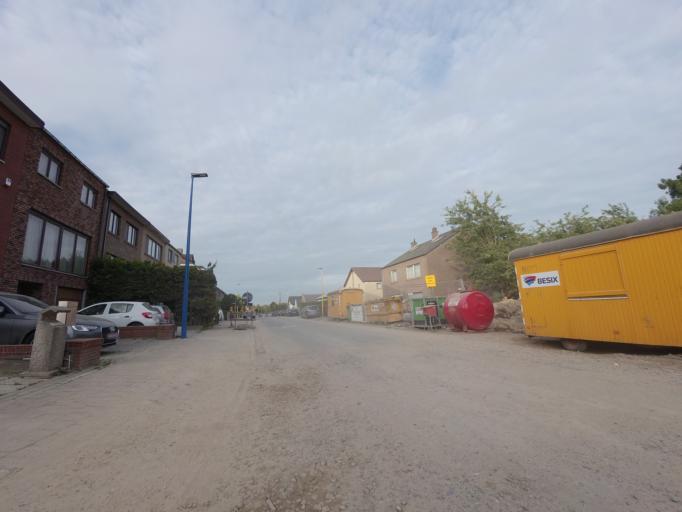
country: BE
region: Flanders
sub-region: Provincie Vlaams-Brabant
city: Grimbergen
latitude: 50.9201
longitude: 4.3909
